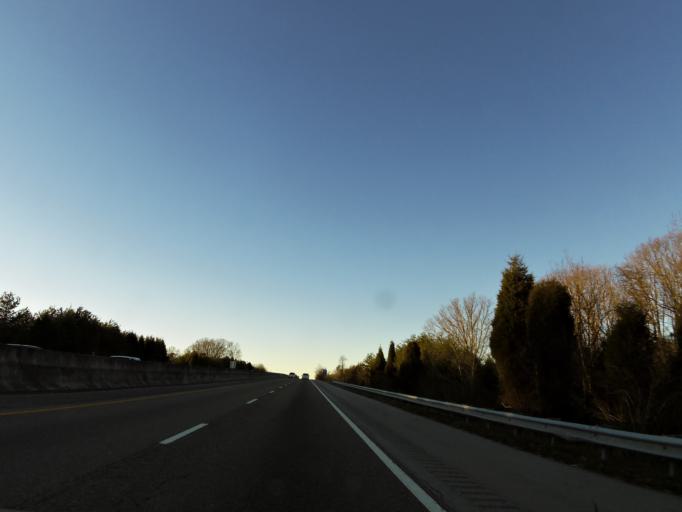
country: US
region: Tennessee
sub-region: Blount County
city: Louisville
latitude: 35.8669
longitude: -84.0827
